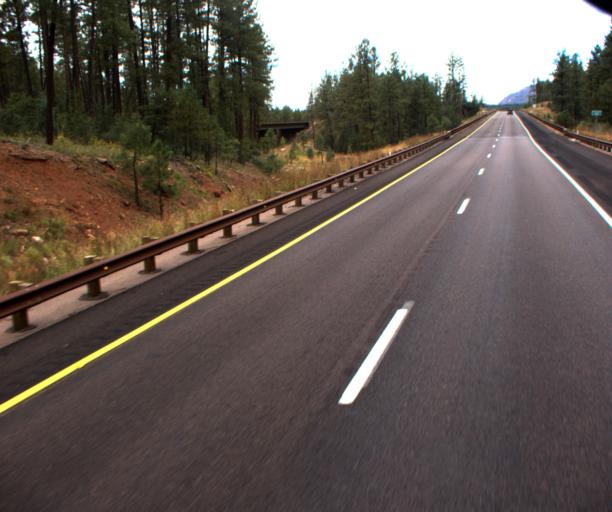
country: US
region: Arizona
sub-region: Gila County
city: Star Valley
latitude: 34.3092
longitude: -111.1092
